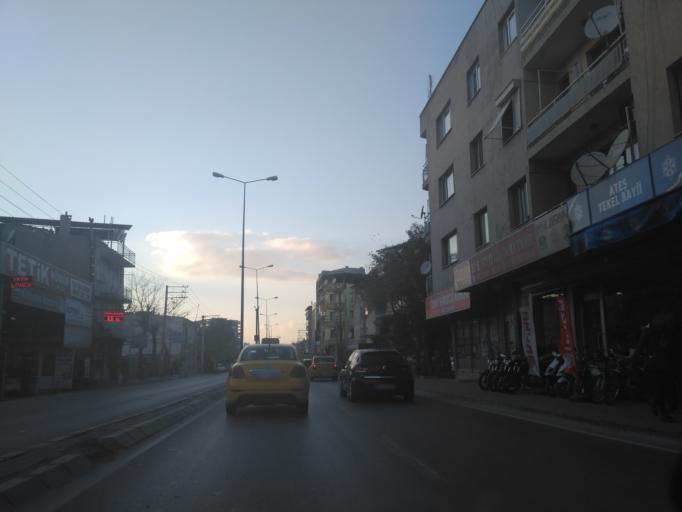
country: TR
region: Izmir
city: Buca
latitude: 38.4299
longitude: 27.2016
